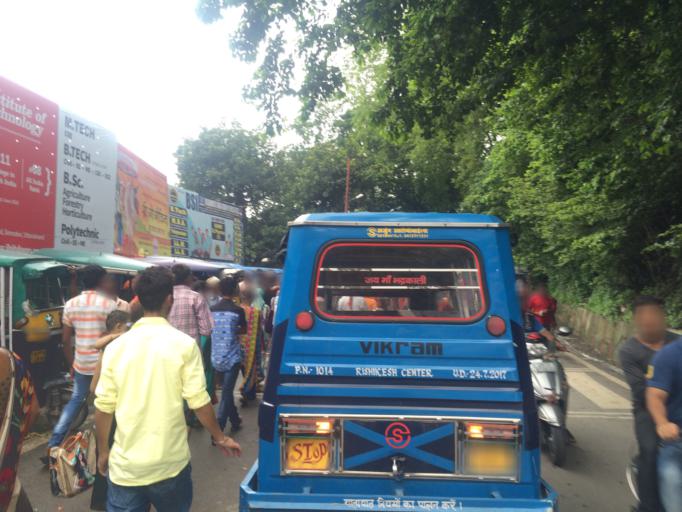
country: IN
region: Uttarakhand
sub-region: Dehradun
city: Rishikesh
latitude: 30.1204
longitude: 78.3071
